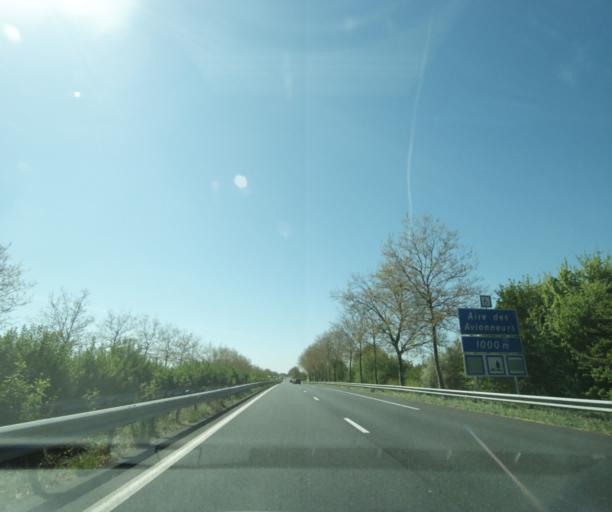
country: FR
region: Centre
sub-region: Departement de l'Indre
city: Montierchaume
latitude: 46.8971
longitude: 1.7315
